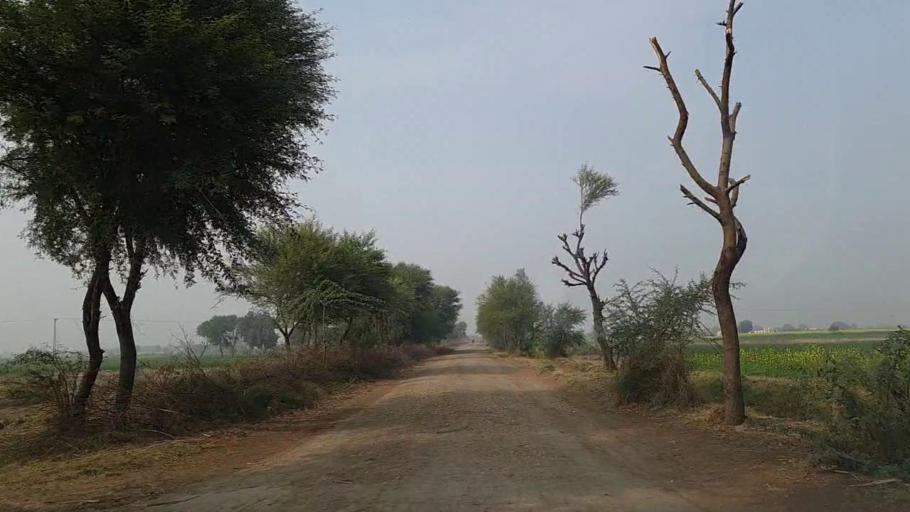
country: PK
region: Sindh
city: Sanghar
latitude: 26.0992
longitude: 68.8968
